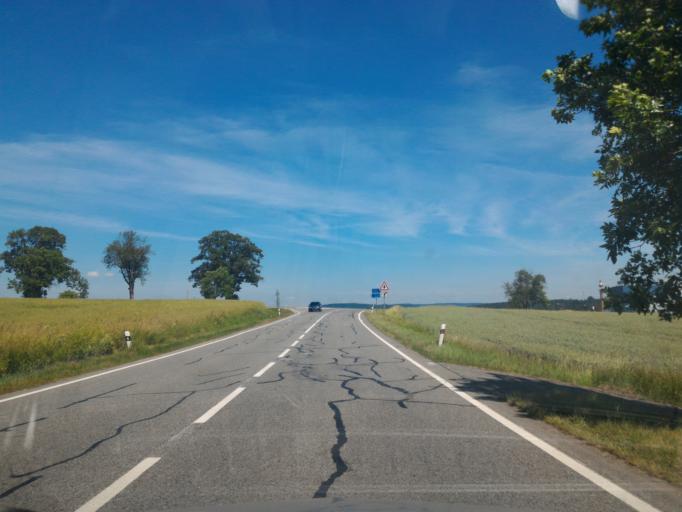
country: CZ
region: Vysocina
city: Dolni Cerekev
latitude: 49.3501
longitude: 15.4861
